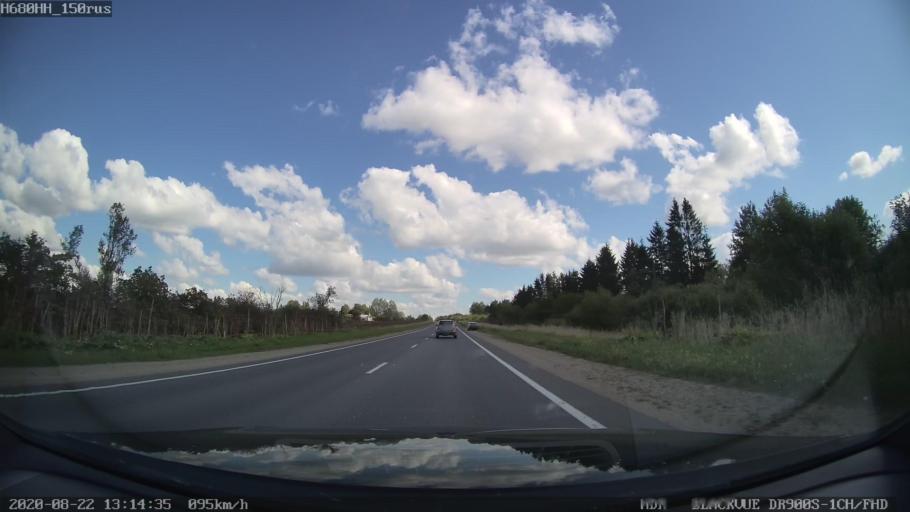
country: RU
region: Tverskaya
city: Bezhetsk
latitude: 57.7554
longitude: 36.6061
